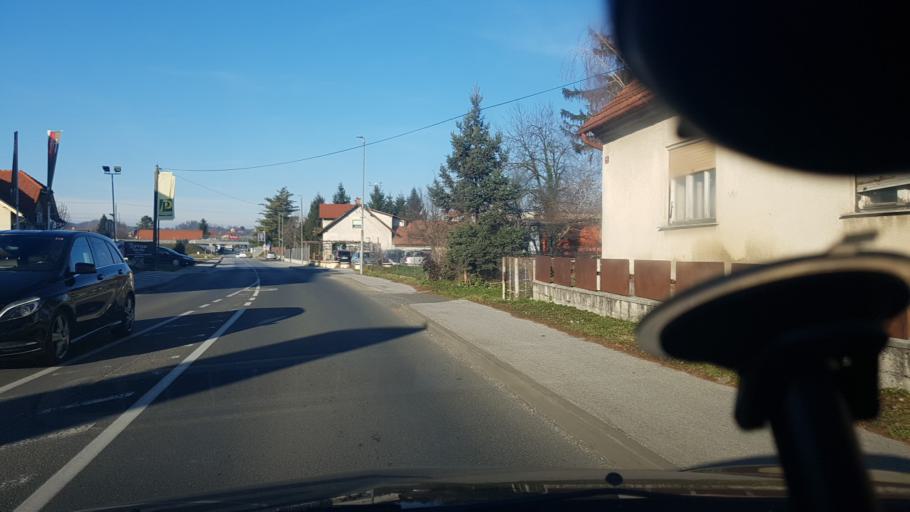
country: SI
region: Ptuj
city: Ptuj
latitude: 46.4088
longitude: 15.8659
